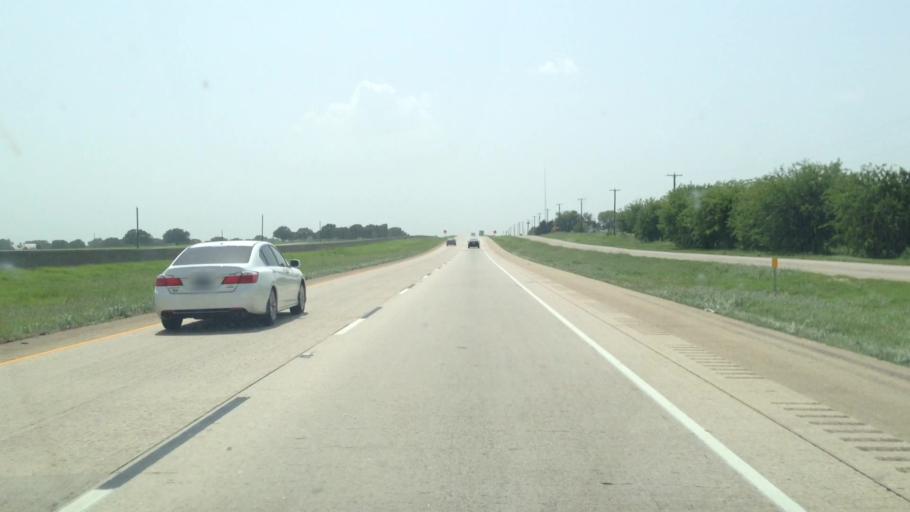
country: US
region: Texas
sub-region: Hopkins County
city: Sulphur Springs
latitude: 33.1209
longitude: -95.6954
